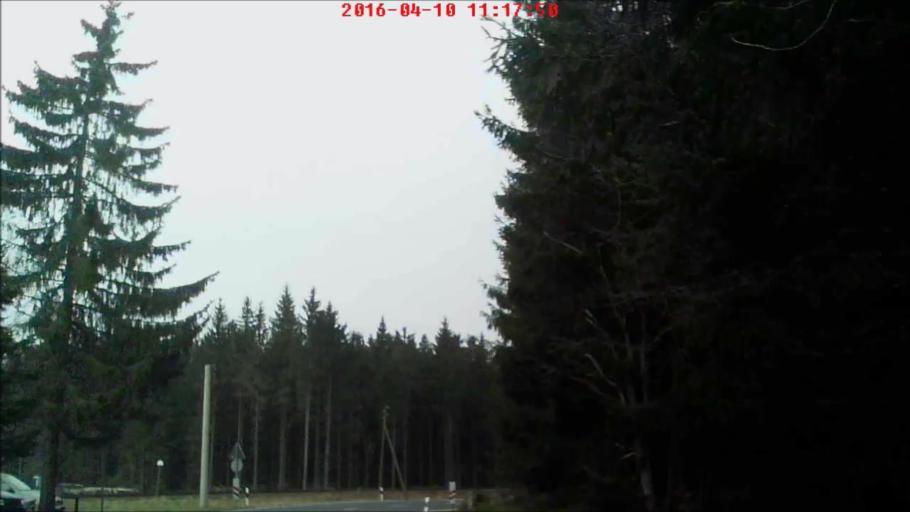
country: DE
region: Thuringia
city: Schmiedefeld am Rennsteig
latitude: 50.6156
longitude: 10.8352
